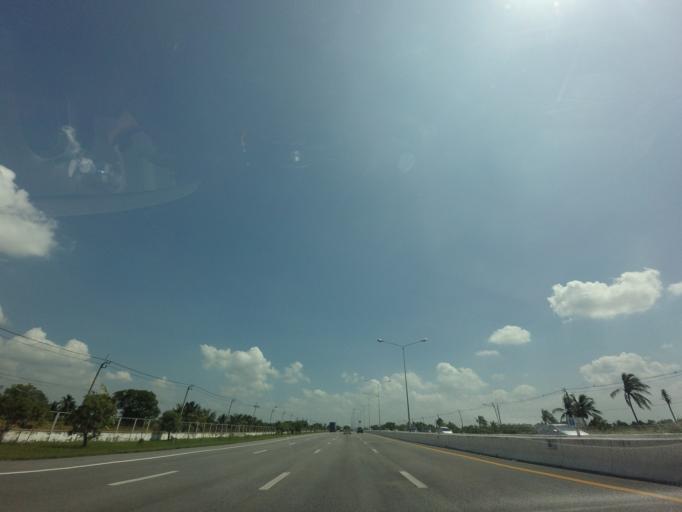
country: TH
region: Samut Prakan
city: Ban Khlong Bang Sao Thong
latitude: 13.6329
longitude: 100.9018
